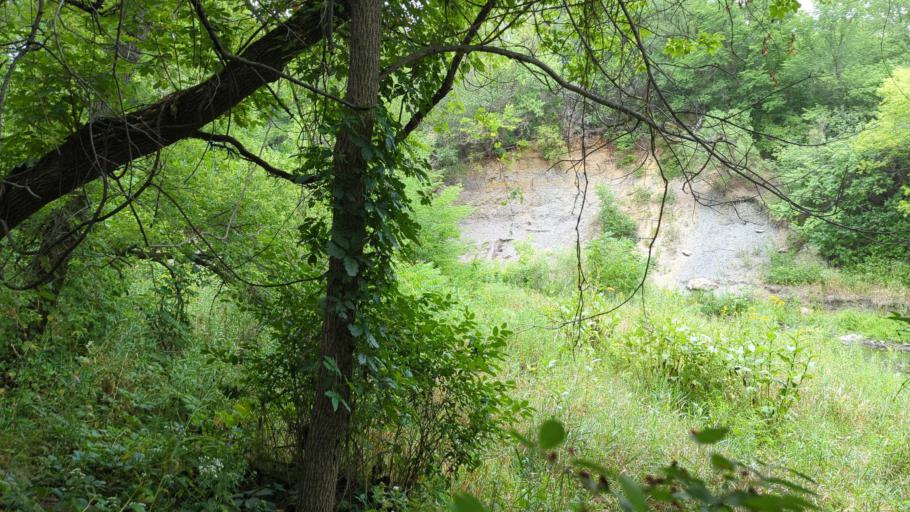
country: US
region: South Dakota
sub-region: Union County
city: Beresford
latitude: 42.9246
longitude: -96.7782
